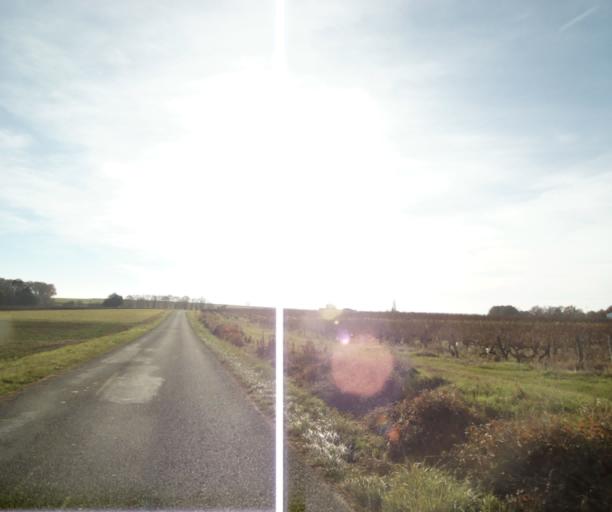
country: FR
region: Poitou-Charentes
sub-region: Departement de la Charente-Maritime
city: Chaniers
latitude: 45.7348
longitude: -0.5485
